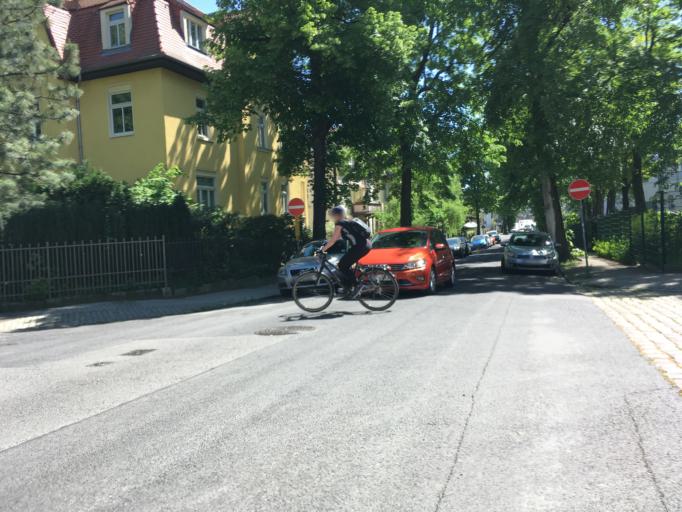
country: DE
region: Saxony
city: Radebeul
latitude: 51.0921
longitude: 13.7017
